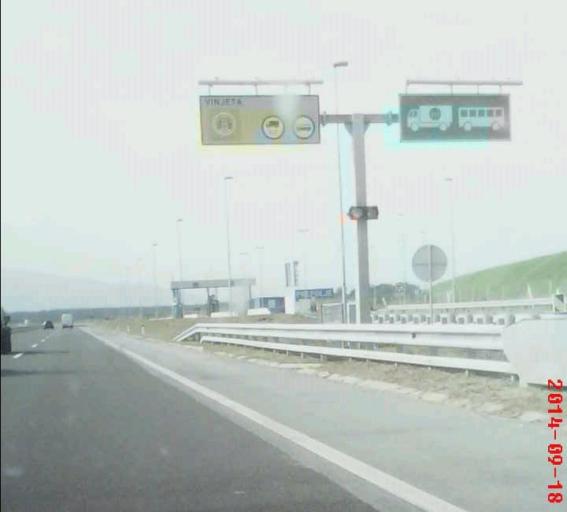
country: SI
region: Starse
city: Starse
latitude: 46.4514
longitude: 15.7620
